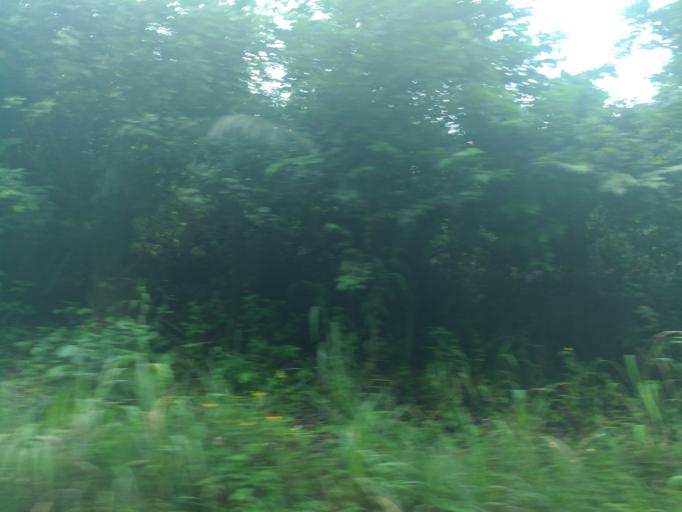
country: NG
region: Lagos
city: Ikorodu
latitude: 6.6664
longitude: 3.6399
